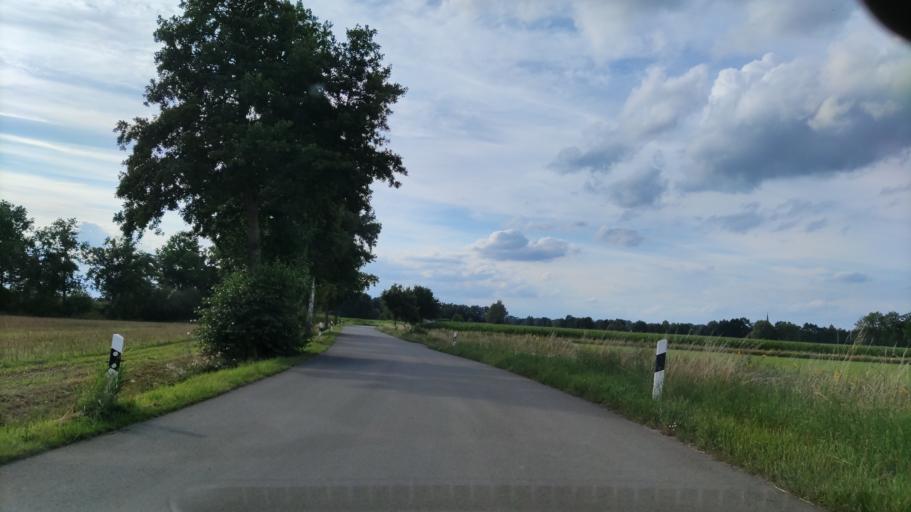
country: DE
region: Lower Saxony
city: Dannenberg
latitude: 53.0875
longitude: 11.1016
